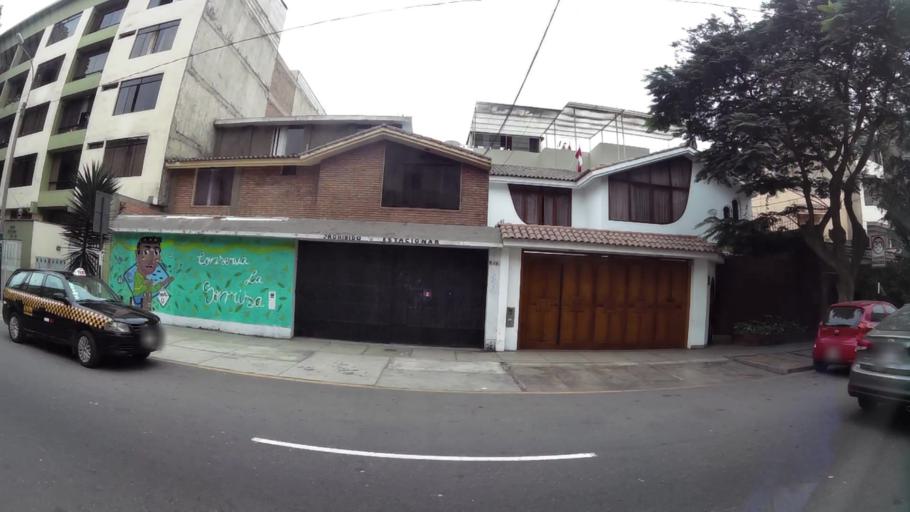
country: PE
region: Lima
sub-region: Lima
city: Surco
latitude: -12.1441
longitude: -77.0009
